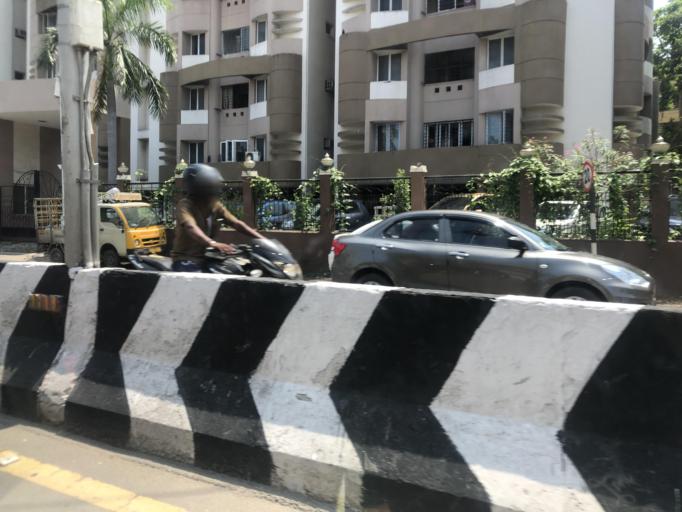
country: IN
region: Tamil Nadu
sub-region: Chennai
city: Gandhi Nagar
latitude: 12.9824
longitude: 80.2594
